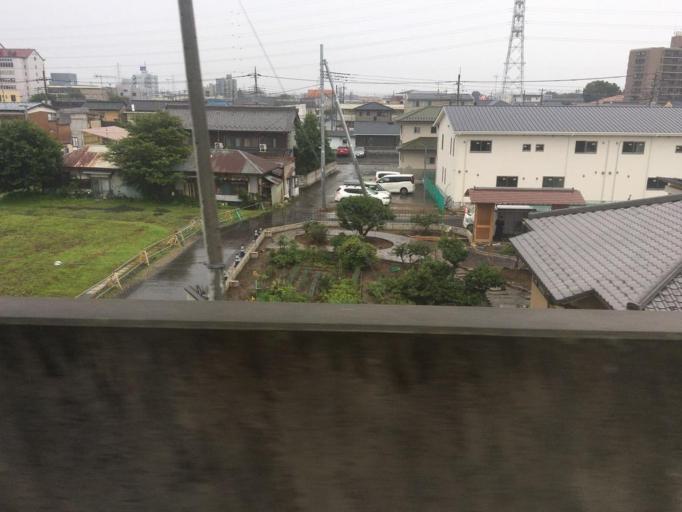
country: JP
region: Gunma
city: Ota
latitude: 36.2945
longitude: 139.3723
